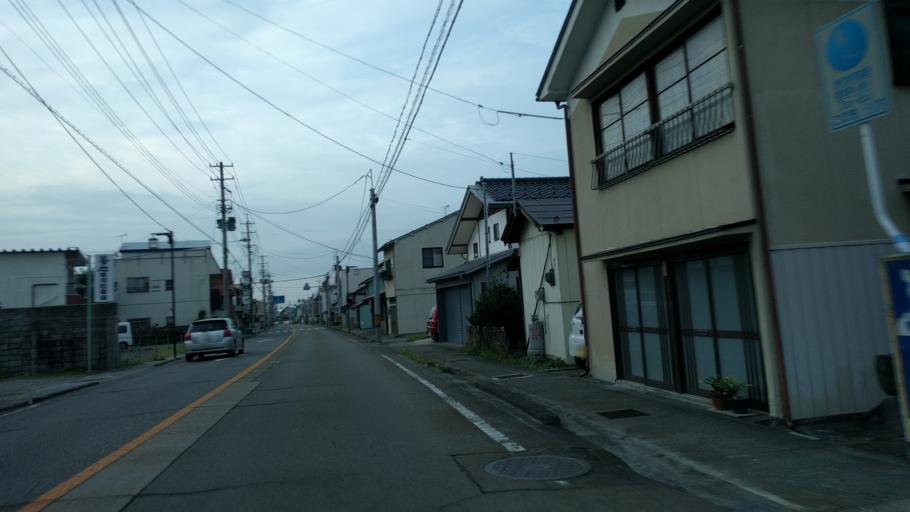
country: JP
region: Fukushima
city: Kitakata
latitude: 37.6570
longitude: 139.8794
